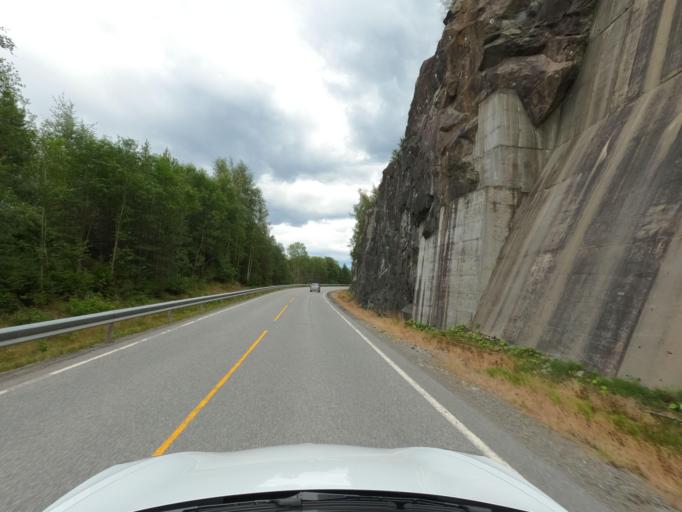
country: NO
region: Telemark
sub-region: Hjartdal
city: Sauland
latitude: 59.8788
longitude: 8.9148
